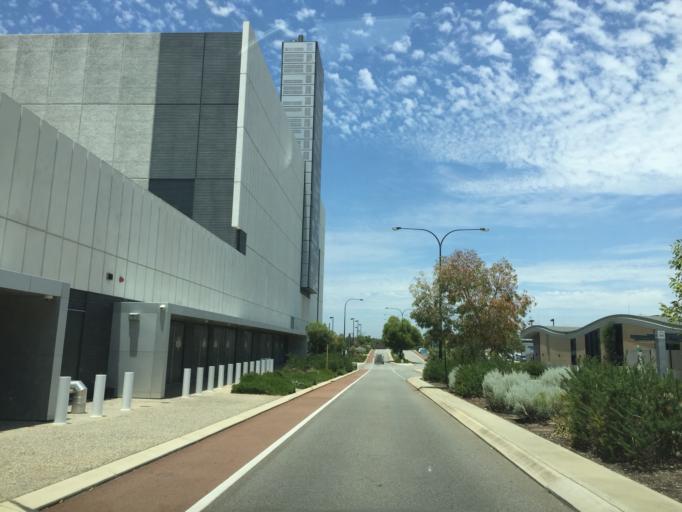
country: AU
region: Western Australia
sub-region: Melville
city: Winthrop
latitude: -32.0703
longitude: 115.8486
